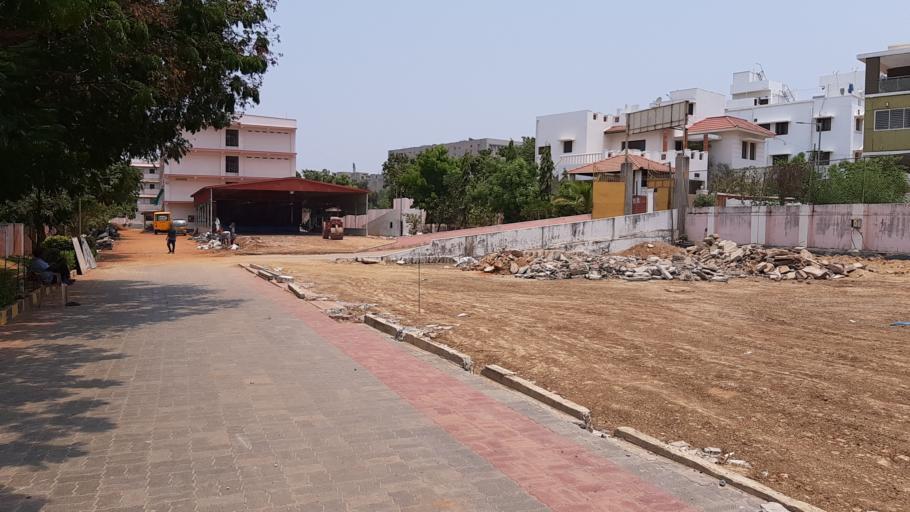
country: IN
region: Tamil Nadu
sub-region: Kancheepuram
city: Saint Thomas Mount
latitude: 13.0245
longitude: 80.1899
